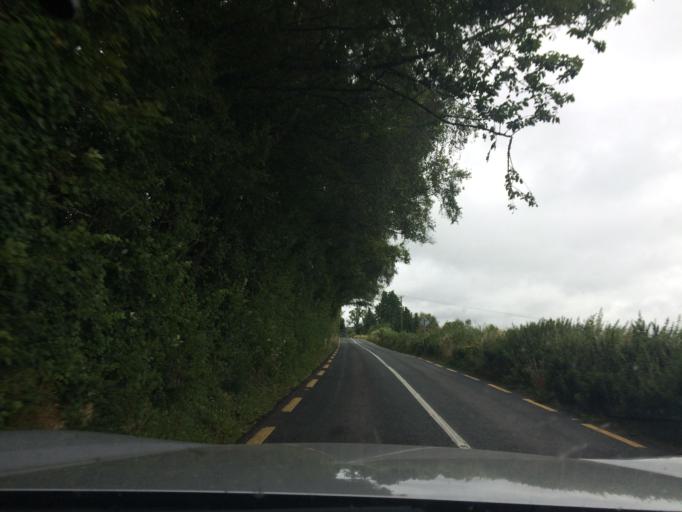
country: IE
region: Munster
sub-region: South Tipperary
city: Cluain Meala
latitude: 52.2923
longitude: -7.7733
